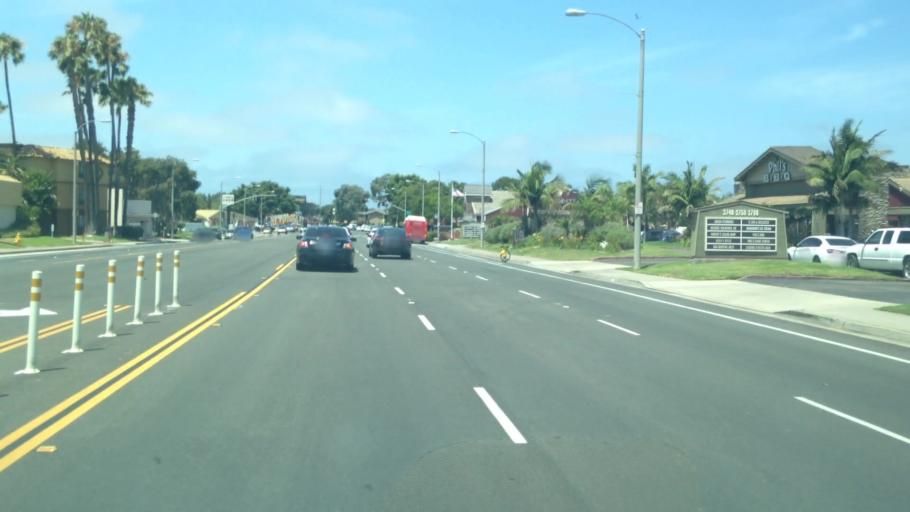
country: US
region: California
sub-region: San Diego County
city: San Diego
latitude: 32.7544
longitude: -117.2153
